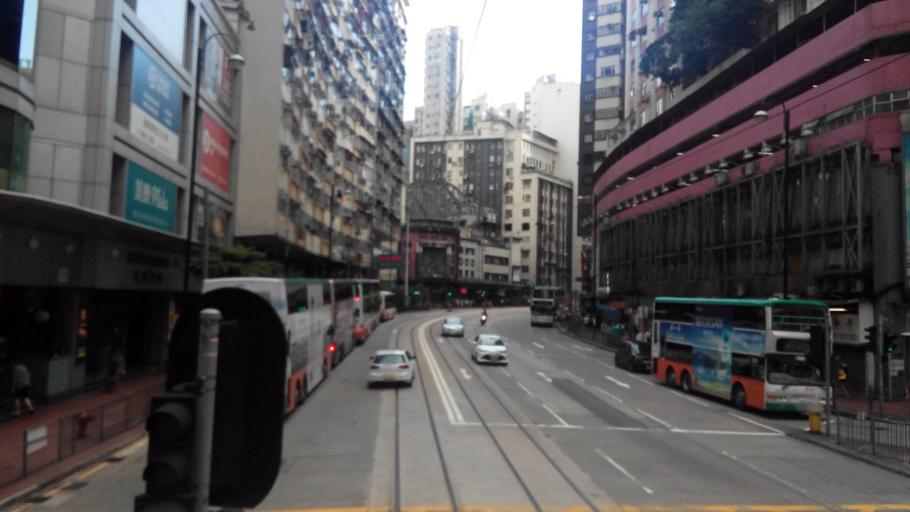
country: HK
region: Wanchai
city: Wan Chai
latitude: 22.2894
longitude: 114.1946
